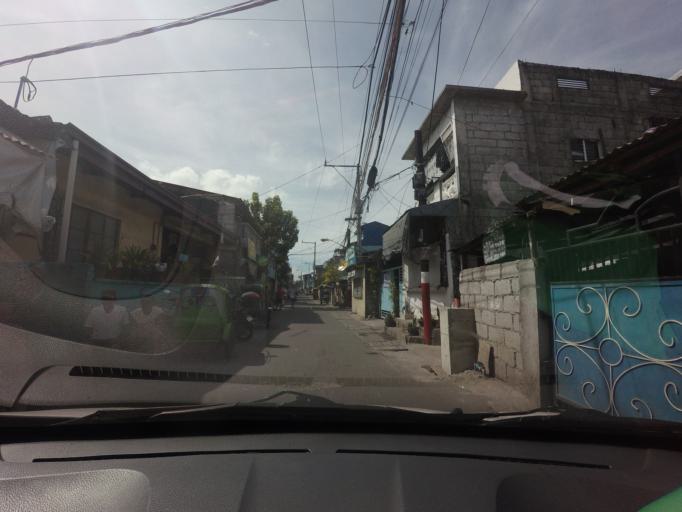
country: PH
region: Calabarzon
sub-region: Province of Rizal
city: Taguig
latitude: 14.5376
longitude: 121.0978
